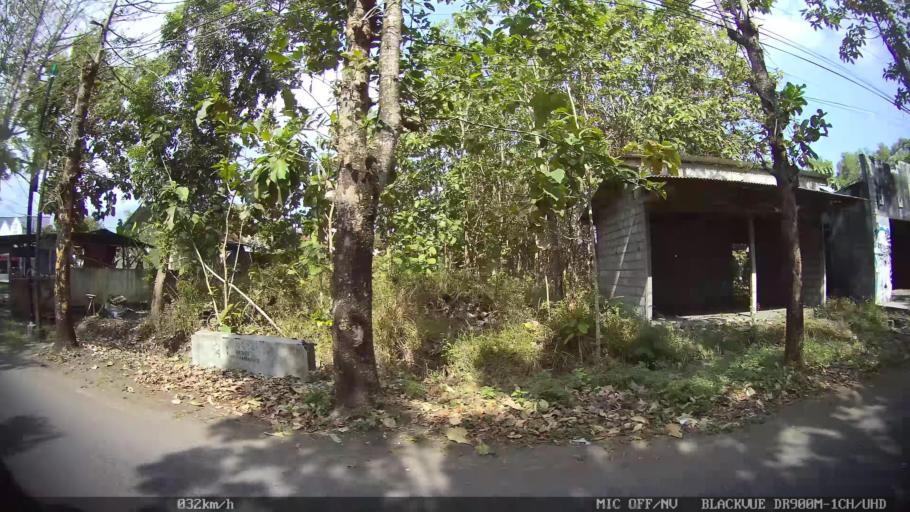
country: ID
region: Daerah Istimewa Yogyakarta
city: Bantul
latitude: -7.8579
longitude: 110.3007
